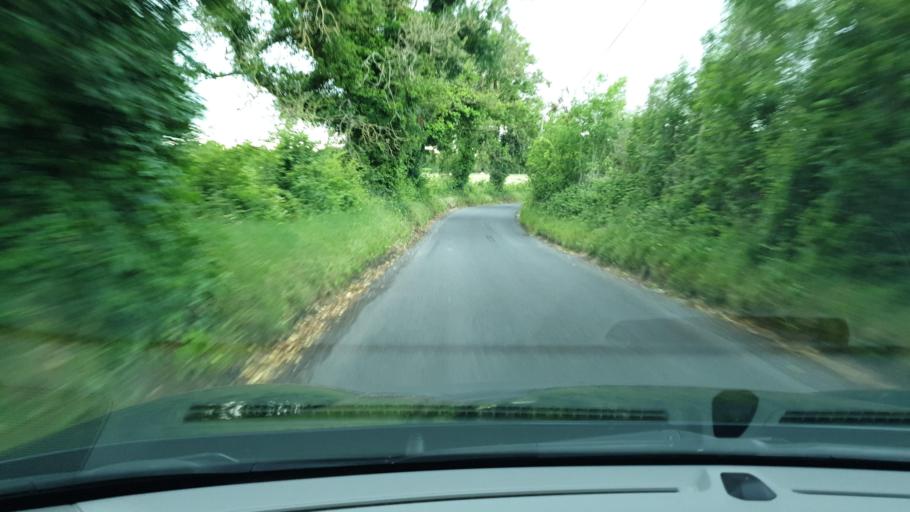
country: IE
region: Leinster
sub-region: An Mhi
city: Navan
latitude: 53.6392
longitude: -6.7189
